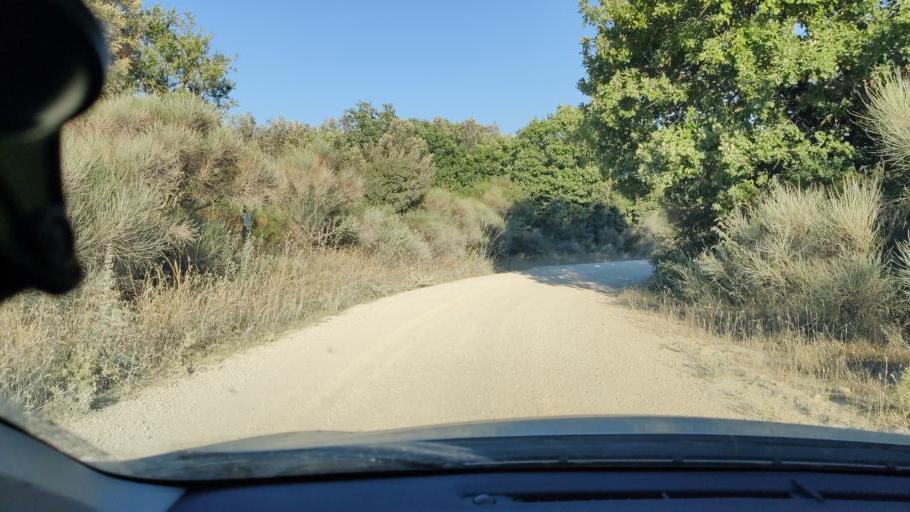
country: IT
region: Umbria
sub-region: Provincia di Terni
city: Amelia
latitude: 42.5385
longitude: 12.3788
